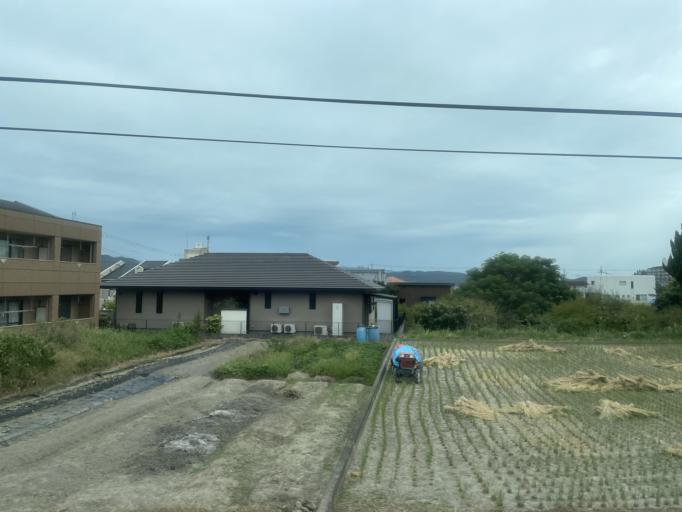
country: JP
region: Wakayama
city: Iwade
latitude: 34.2686
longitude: 135.2378
